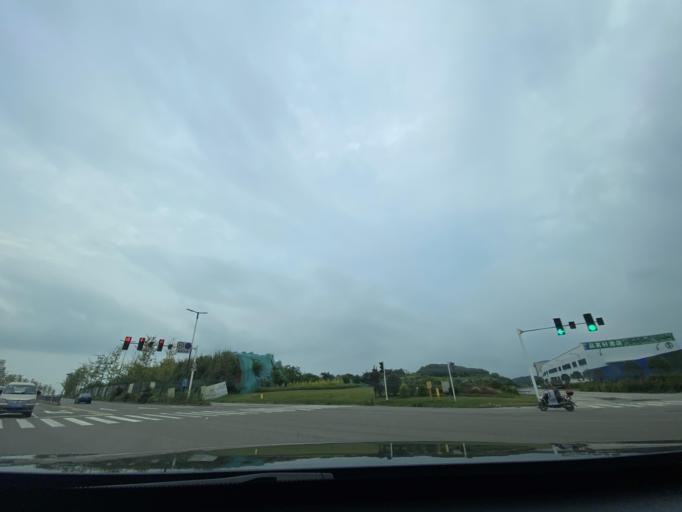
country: CN
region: Sichuan
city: Jiancheng
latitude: 30.4947
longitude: 104.4504
